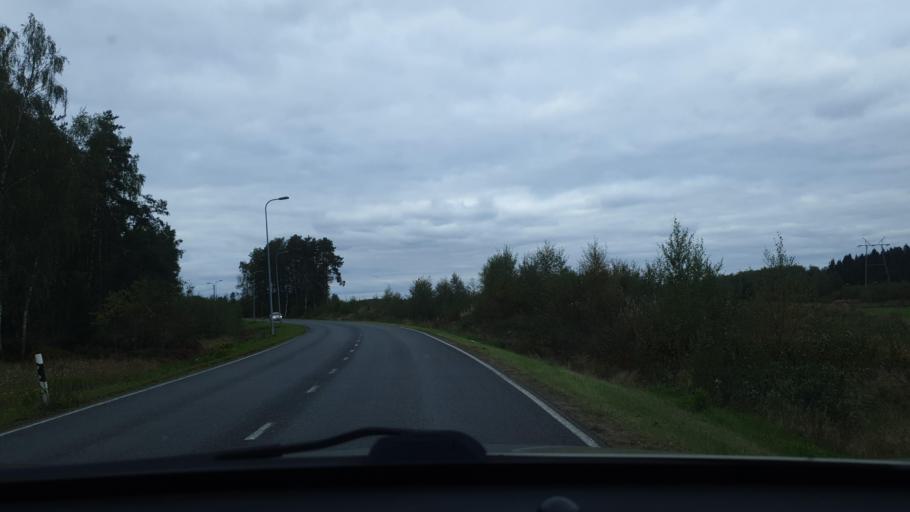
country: FI
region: Ostrobothnia
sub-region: Vaasa
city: Teeriniemi
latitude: 63.0960
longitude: 21.6984
